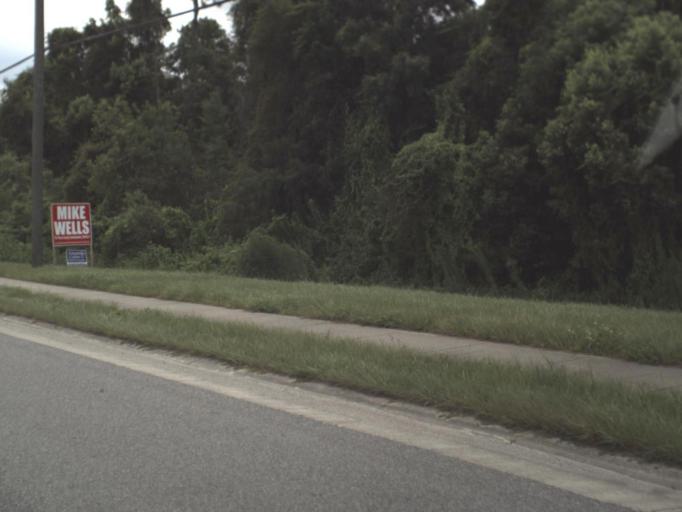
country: US
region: Florida
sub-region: Pasco County
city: Land O' Lakes
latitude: 28.1868
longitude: -82.4531
